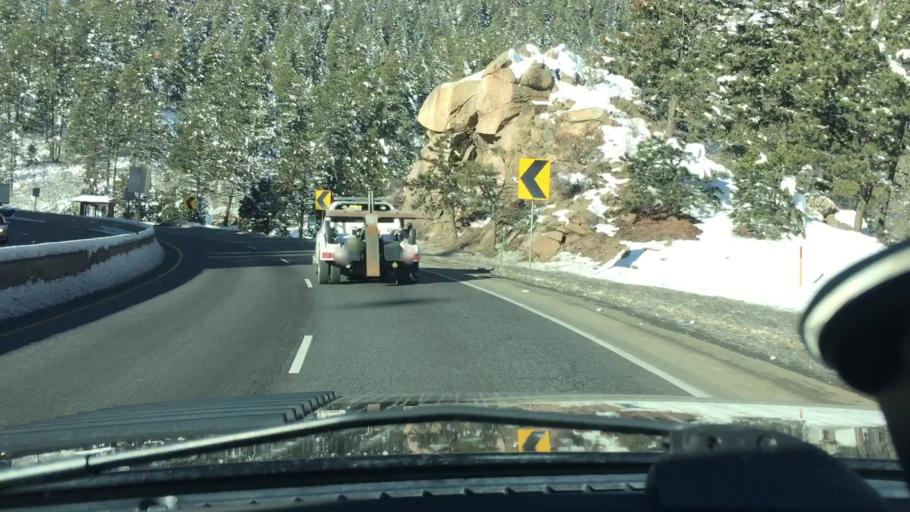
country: US
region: Colorado
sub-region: Jefferson County
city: Indian Hills
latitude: 39.6198
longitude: -105.2271
